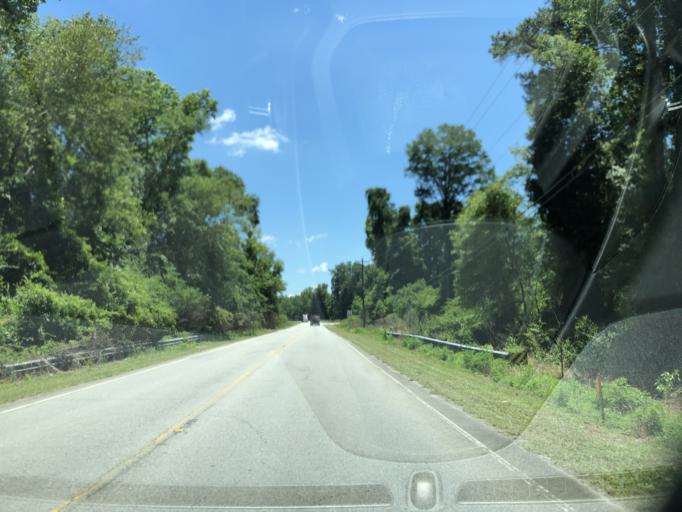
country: US
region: South Carolina
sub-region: Orangeburg County
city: Branchville
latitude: 33.2498
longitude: -80.8062
